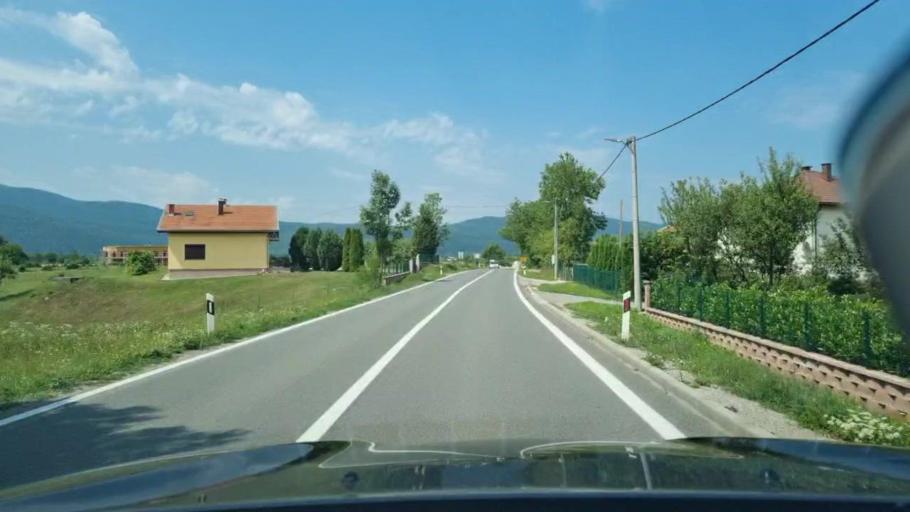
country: BA
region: Federation of Bosnia and Herzegovina
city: Izacic
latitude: 44.8779
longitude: 15.7728
